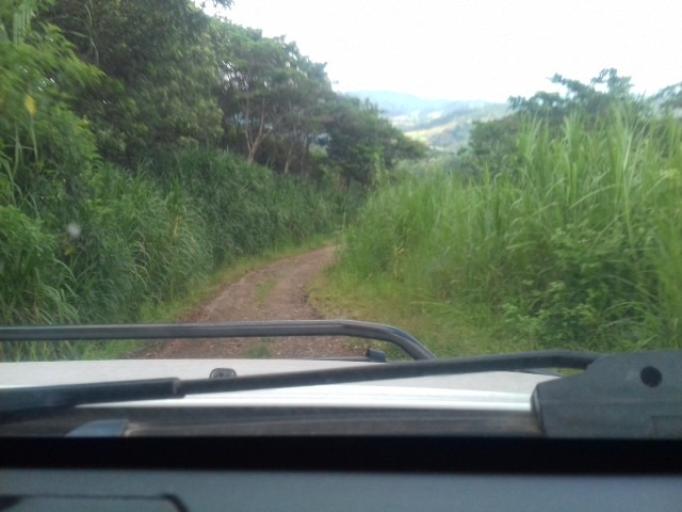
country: NI
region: Atlantico Norte (RAAN)
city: Waslala
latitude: 13.2089
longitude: -85.5798
